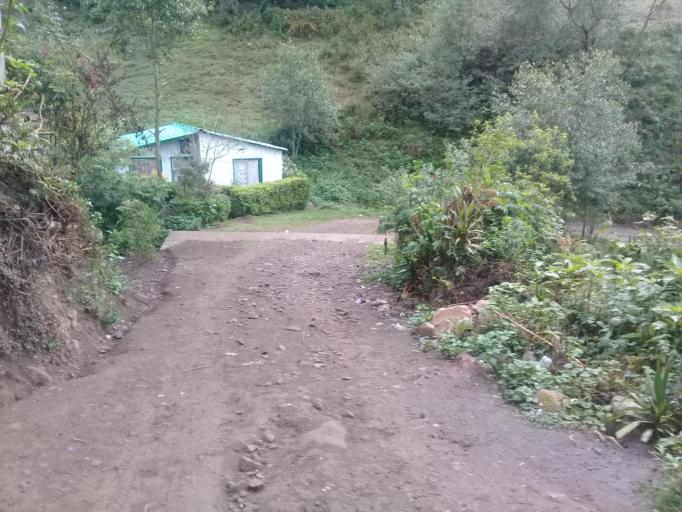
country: MX
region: Veracruz
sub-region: Mariano Escobedo
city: San Isidro el Berro
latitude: 18.9583
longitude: -97.1963
